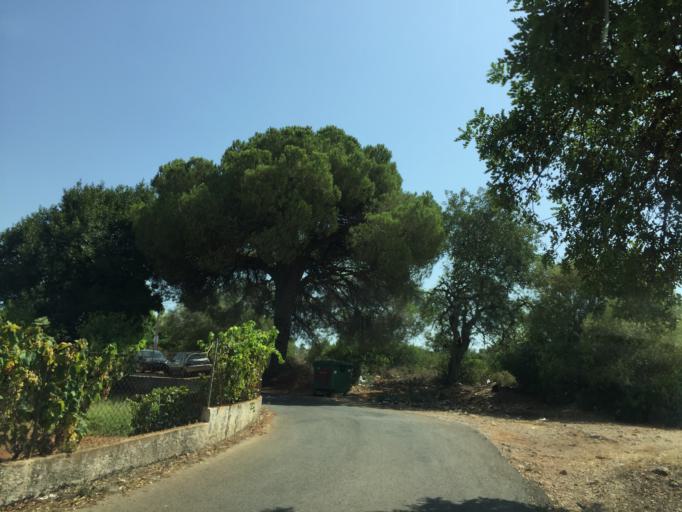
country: PT
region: Faro
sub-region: Albufeira
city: Ferreiras
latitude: 37.1212
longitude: -8.1968
